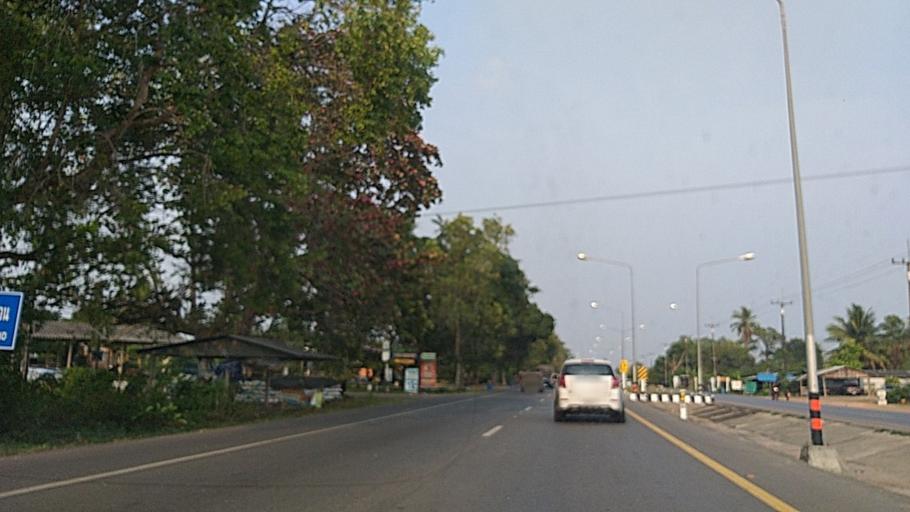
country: TH
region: Chanthaburi
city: Khlung
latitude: 12.4519
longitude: 102.2500
